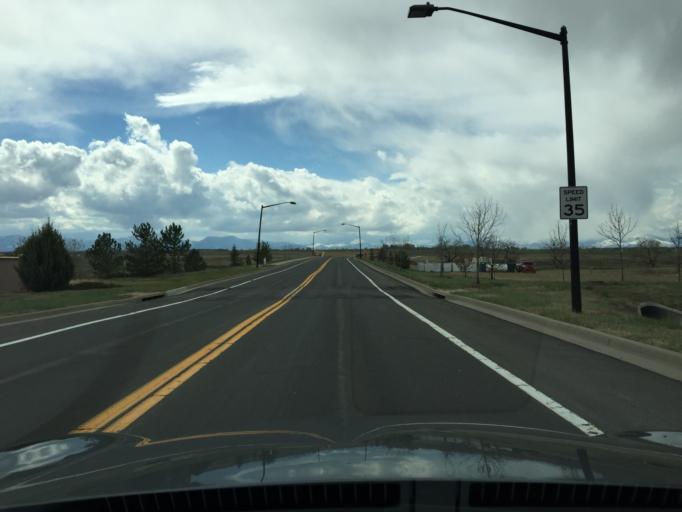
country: US
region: Colorado
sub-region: Boulder County
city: Erie
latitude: 40.0209
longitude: -105.0436
